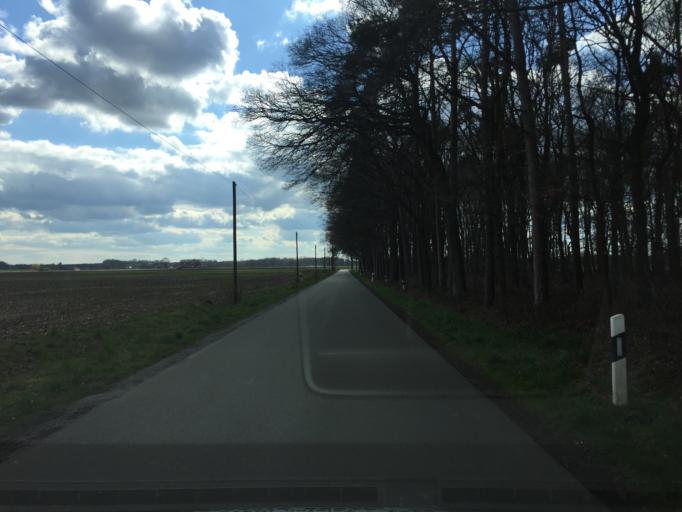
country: DE
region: Lower Saxony
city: Engeln
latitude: 52.7728
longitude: 8.9371
